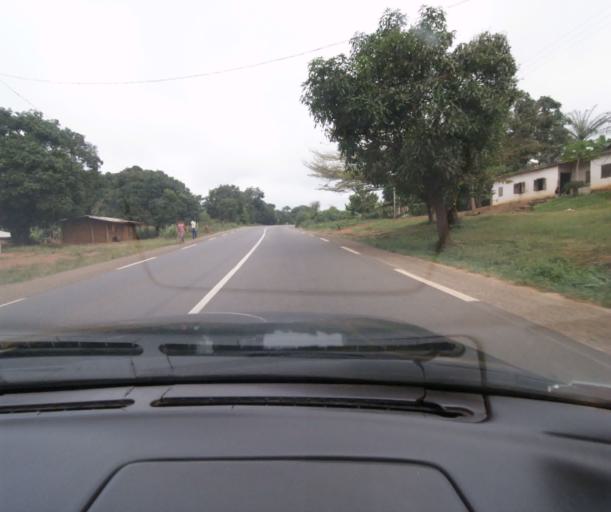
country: CM
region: Centre
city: Obala
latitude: 4.1878
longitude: 11.4580
